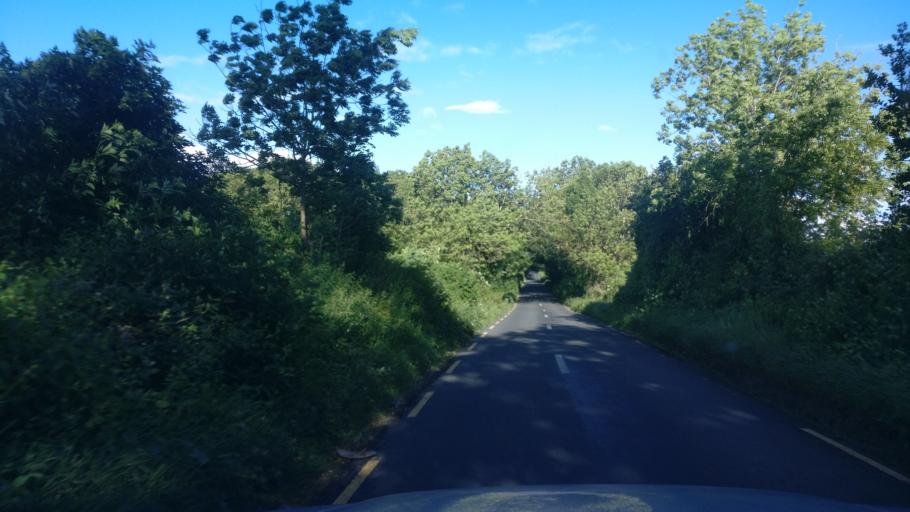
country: IE
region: Connaught
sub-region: County Galway
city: Ballinasloe
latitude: 53.2253
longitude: -8.2238
